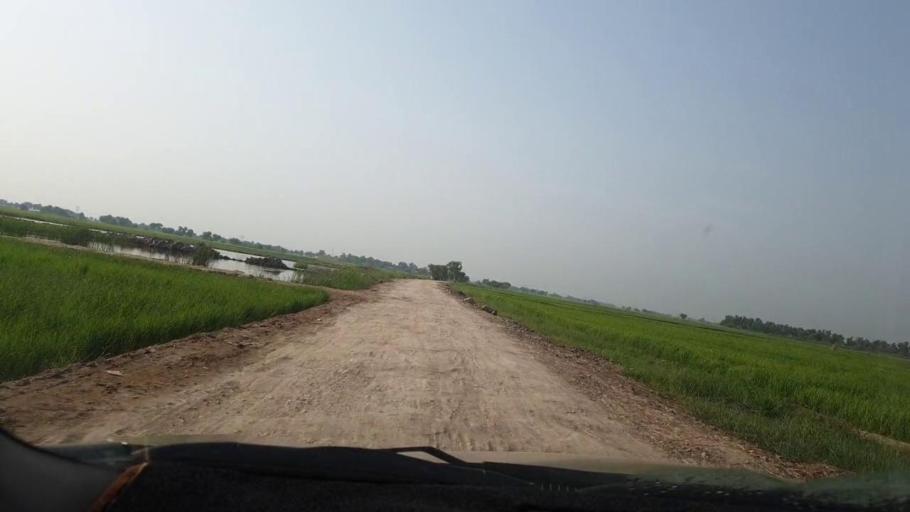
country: PK
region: Sindh
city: Goth Garelo
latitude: 27.4718
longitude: 68.0880
